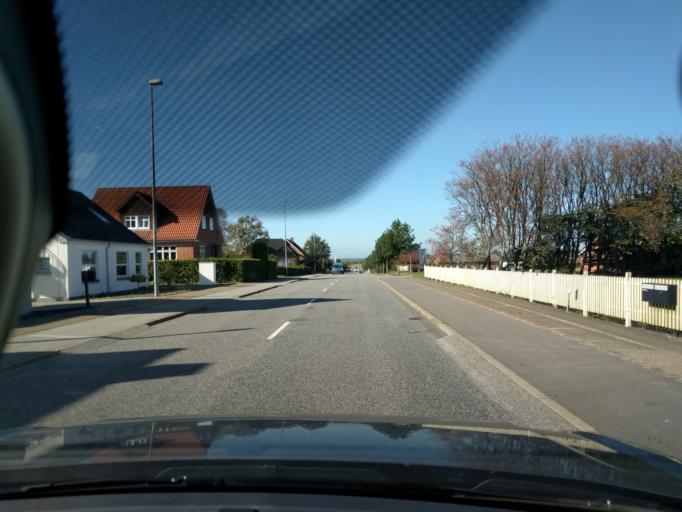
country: DK
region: North Denmark
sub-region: Vesthimmerland Kommune
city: Alestrup
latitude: 56.7093
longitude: 9.6253
